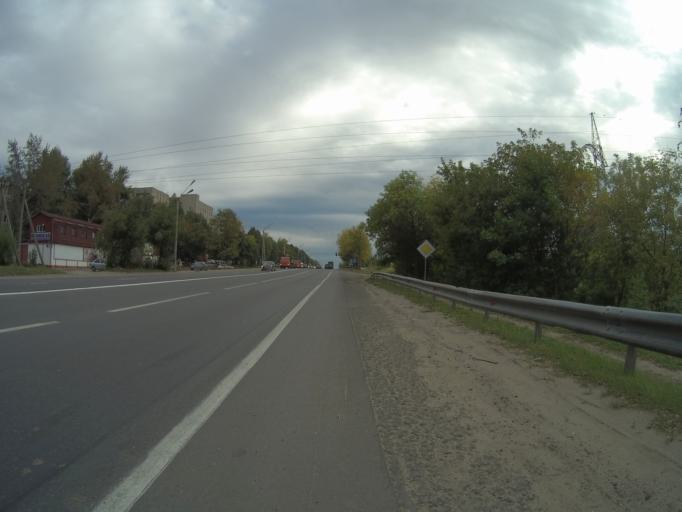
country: RU
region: Vladimir
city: Vladimir
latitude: 56.1408
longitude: 40.3548
